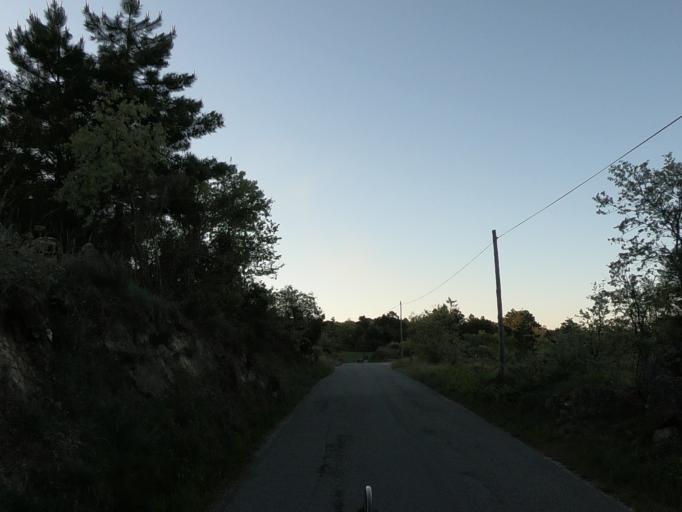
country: PT
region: Vila Real
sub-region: Sabrosa
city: Sabrosa
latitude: 41.3390
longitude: -7.6231
